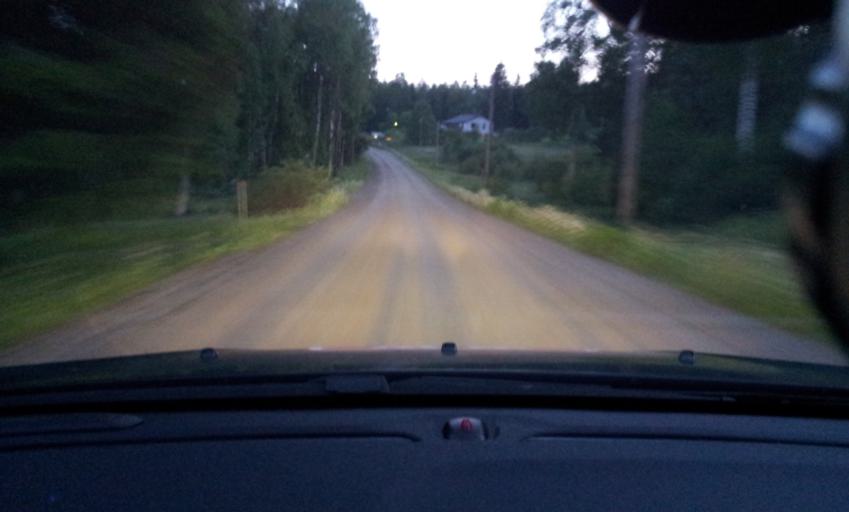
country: SE
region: Jaemtland
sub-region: Braecke Kommun
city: Braecke
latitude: 62.7200
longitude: 15.5817
